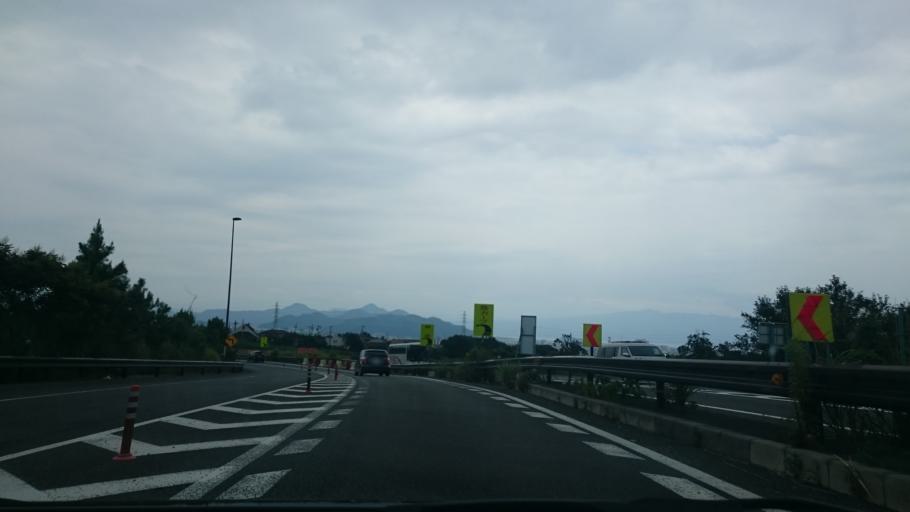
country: JP
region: Shizuoka
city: Numazu
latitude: 35.1416
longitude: 138.8630
